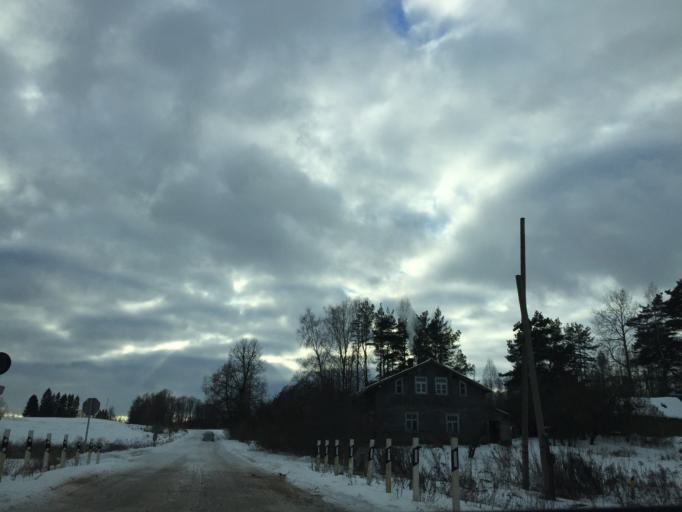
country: LV
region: Lielvarde
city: Lielvarde
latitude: 56.5812
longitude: 24.7350
